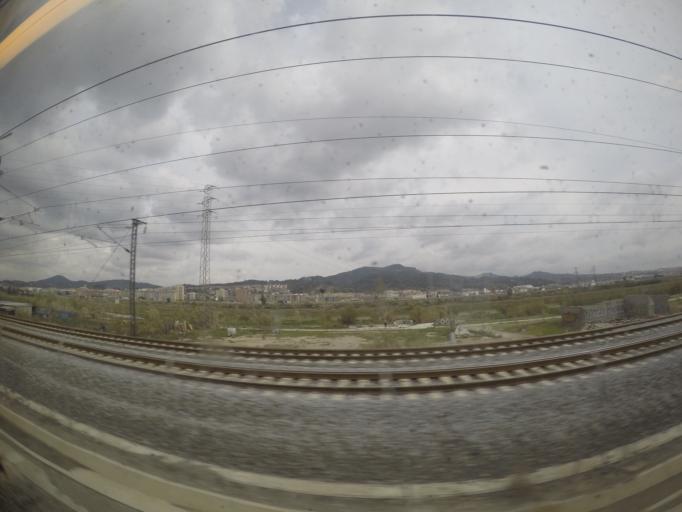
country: ES
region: Catalonia
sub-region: Provincia de Barcelona
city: Sant Vicenc dels Horts
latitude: 41.4012
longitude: 2.0143
